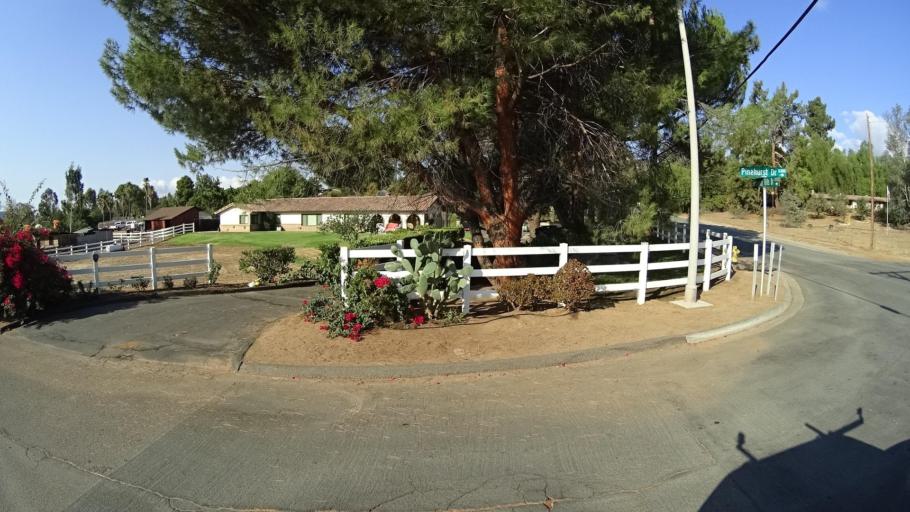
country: US
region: California
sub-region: San Diego County
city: Eucalyptus Hills
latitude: 32.8824
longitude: -116.9422
